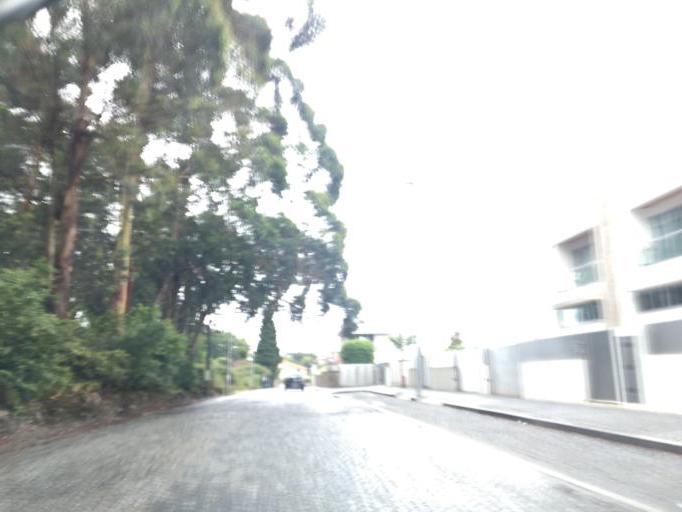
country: PT
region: Porto
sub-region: Maia
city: Nogueira
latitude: 41.2488
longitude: -8.5958
